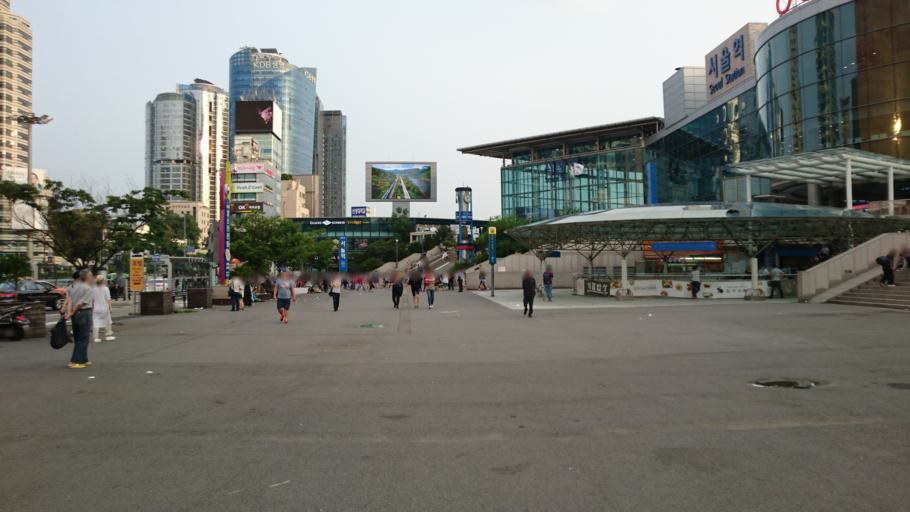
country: KR
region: Seoul
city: Seoul
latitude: 37.5554
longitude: 126.9719
